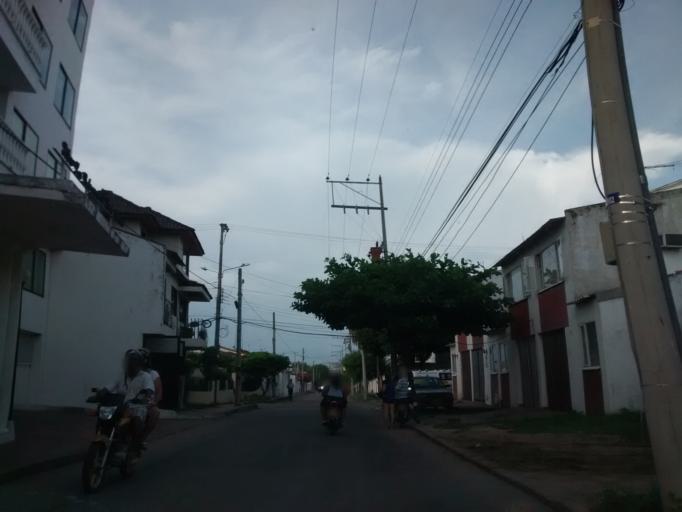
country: CO
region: Cundinamarca
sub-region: Girardot
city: Girardot City
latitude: 4.3065
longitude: -74.8008
